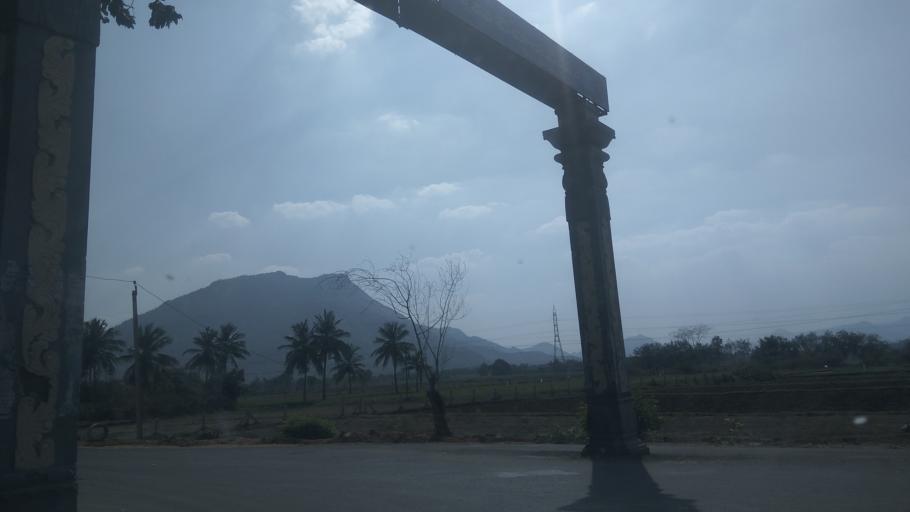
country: IN
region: Andhra Pradesh
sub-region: Chittoor
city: Renigunta
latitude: 13.5546
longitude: 79.4828
